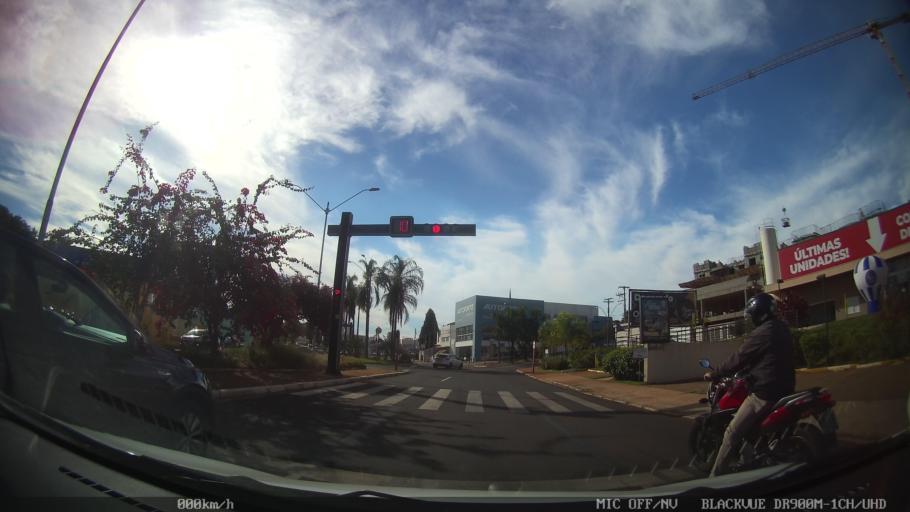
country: BR
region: Sao Paulo
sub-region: Araraquara
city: Araraquara
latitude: -21.8019
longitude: -48.1731
